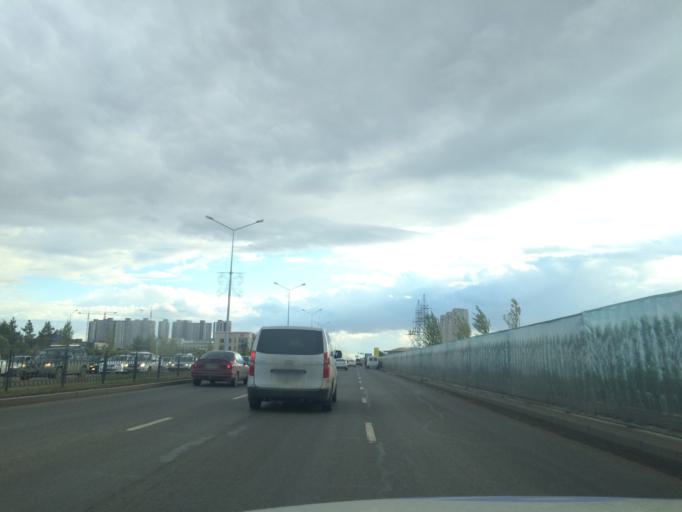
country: KZ
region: Astana Qalasy
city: Astana
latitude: 51.1258
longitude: 71.4040
